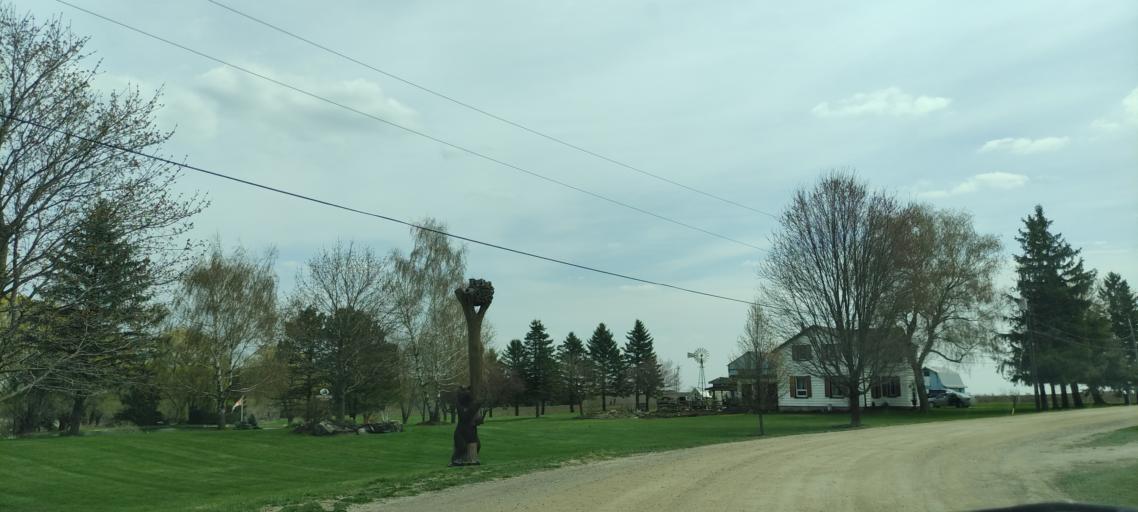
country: CA
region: Ontario
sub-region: Oxford County
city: Woodstock
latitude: 43.2835
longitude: -80.7080
